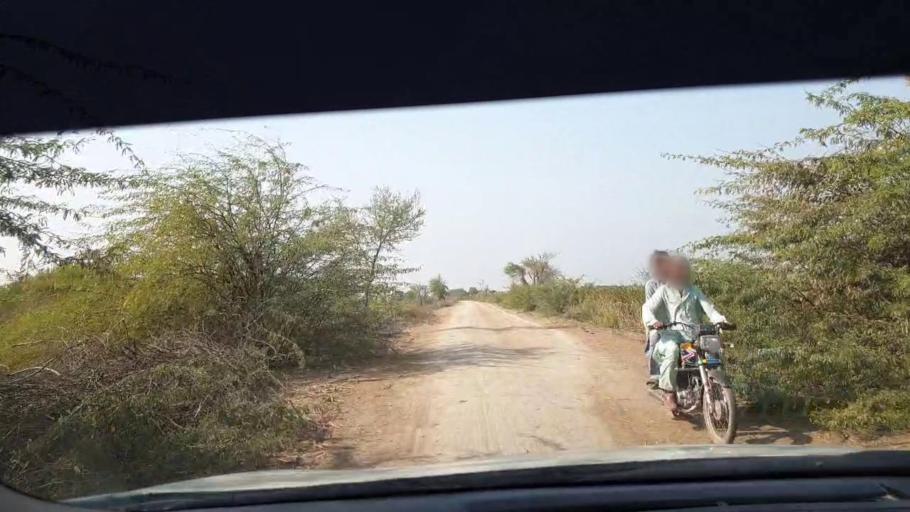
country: PK
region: Sindh
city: Tando Adam
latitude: 25.8388
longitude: 68.7212
